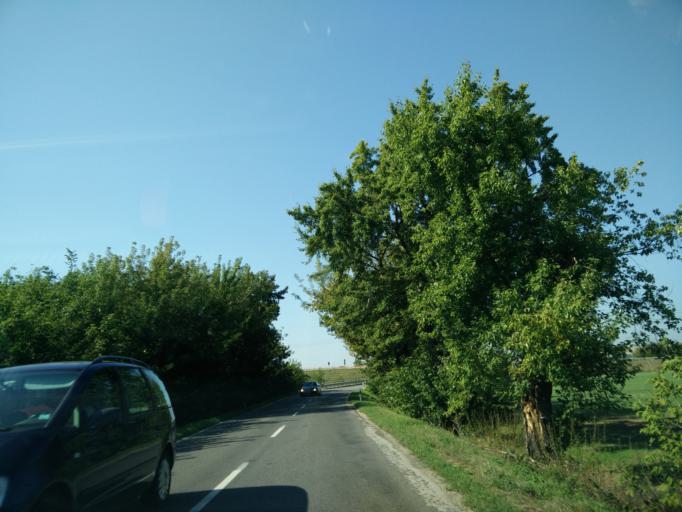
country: SK
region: Nitriansky
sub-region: Okres Nitra
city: Nitra
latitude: 48.3577
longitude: 18.0535
